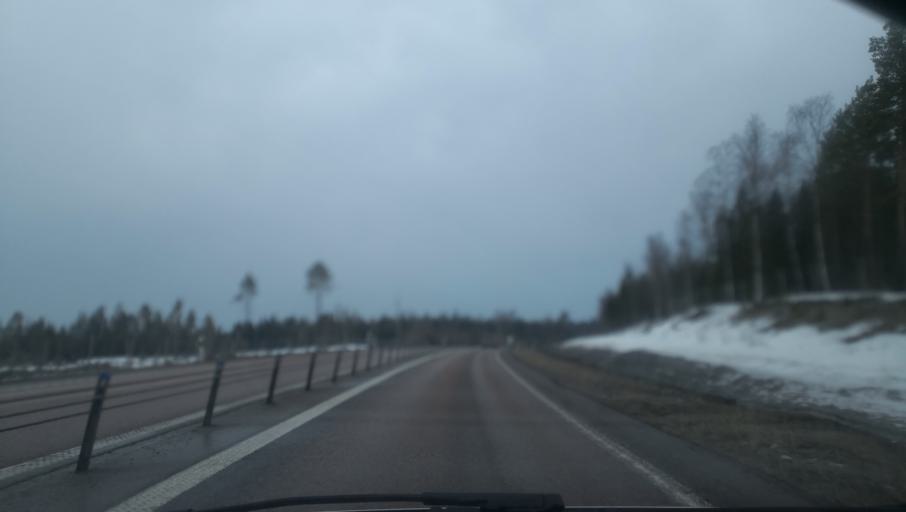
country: SE
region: Vaesternorrland
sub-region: Haernoesands Kommun
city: Haernoesand
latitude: 62.5654
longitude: 17.7326
